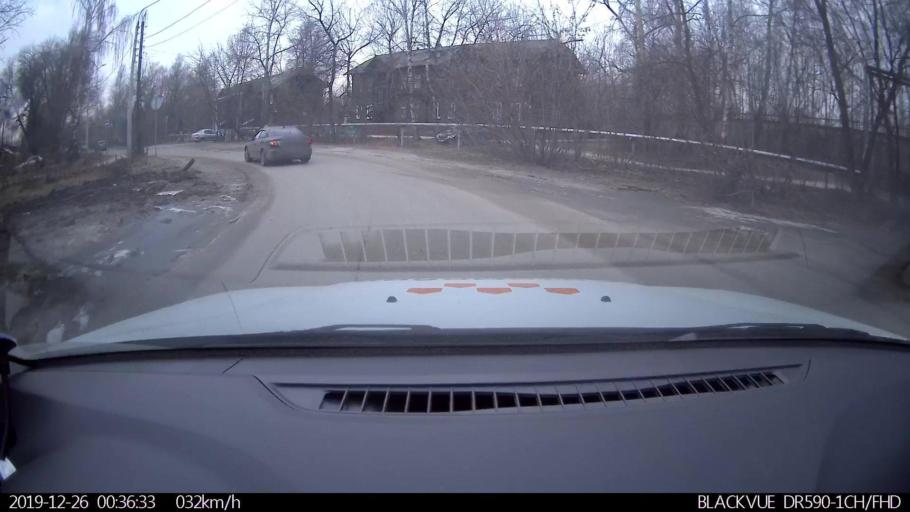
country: RU
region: Nizjnij Novgorod
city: Nizhniy Novgorod
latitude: 56.2926
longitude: 43.9071
